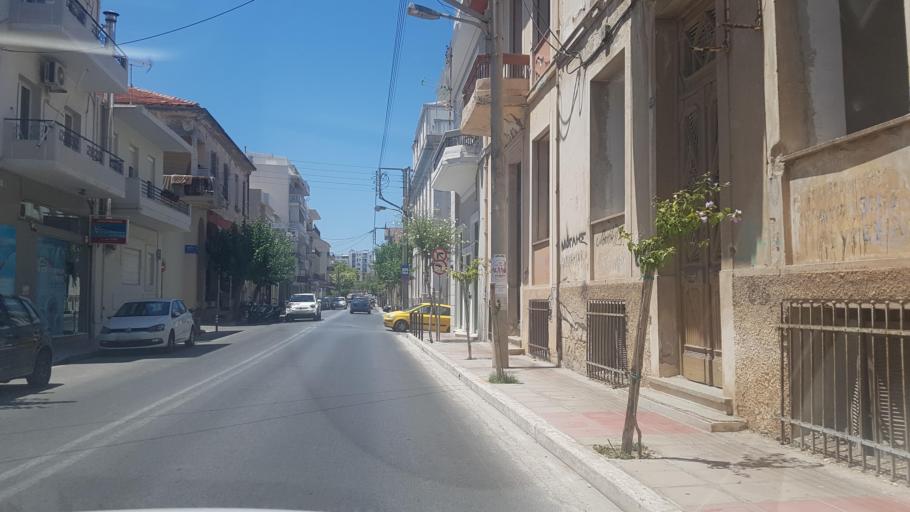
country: GR
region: Crete
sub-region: Nomos Chanias
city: Chania
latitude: 35.5151
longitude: 24.0288
